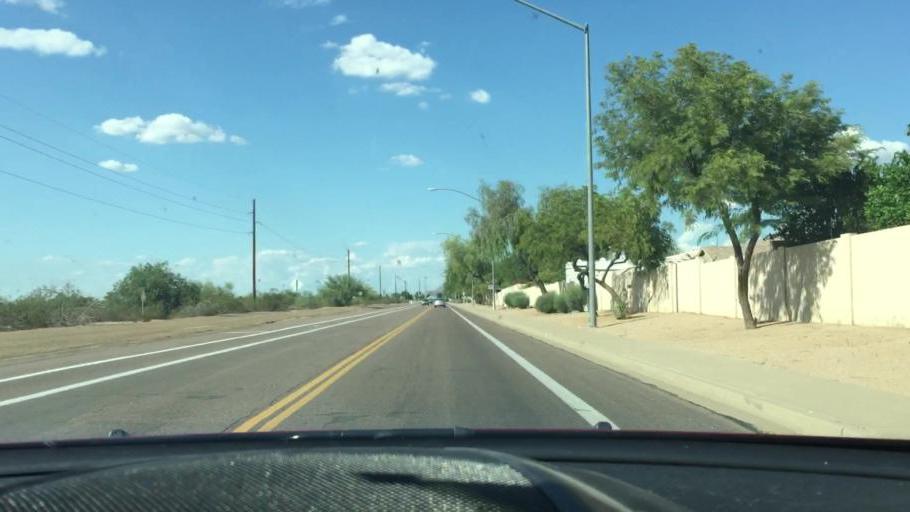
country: US
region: Arizona
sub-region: Pinal County
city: Apache Junction
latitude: 33.4311
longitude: -111.6591
